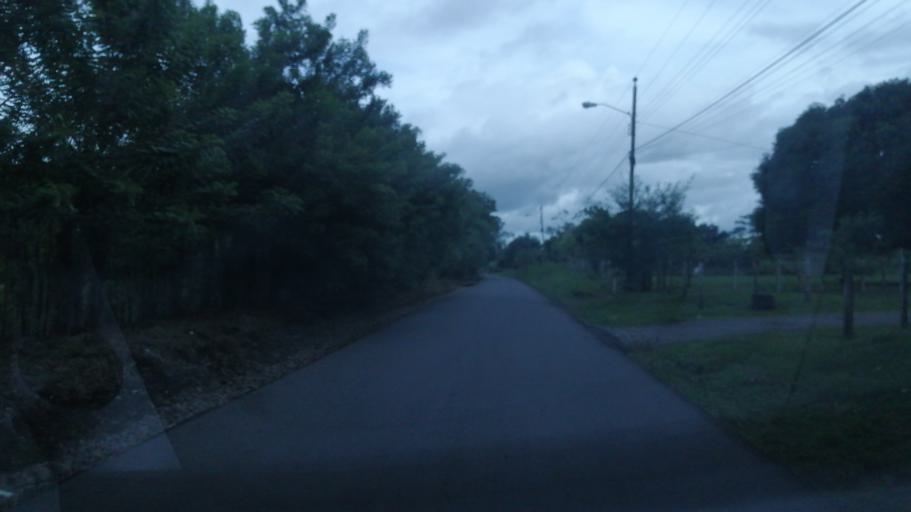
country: PA
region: Chiriqui
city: Tijera
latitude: 8.4511
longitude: -82.5254
